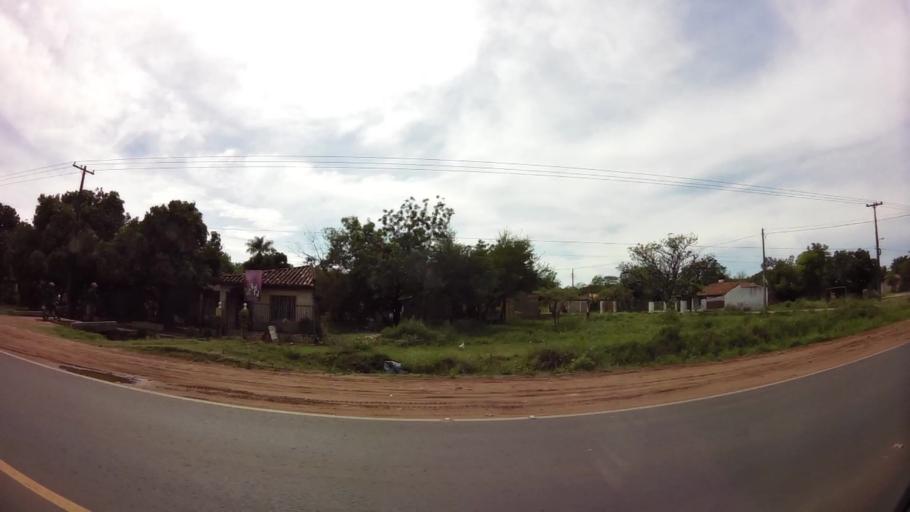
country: PY
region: Central
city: Limpio
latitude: -25.1516
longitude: -57.4729
